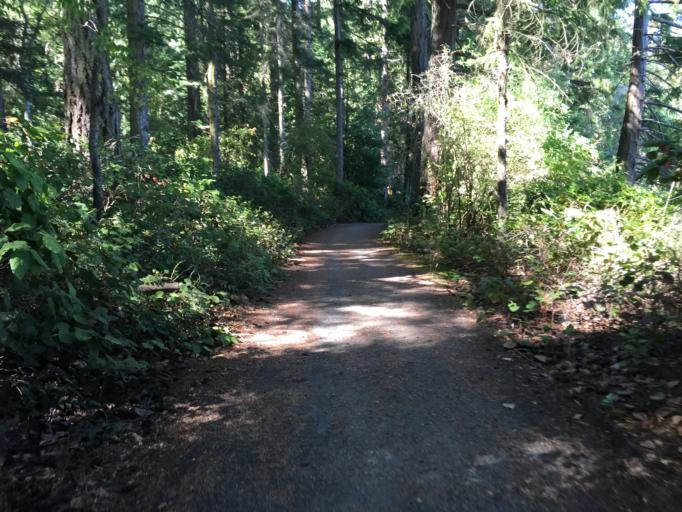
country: CA
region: British Columbia
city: Nanaimo
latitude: 49.1941
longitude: -123.9277
